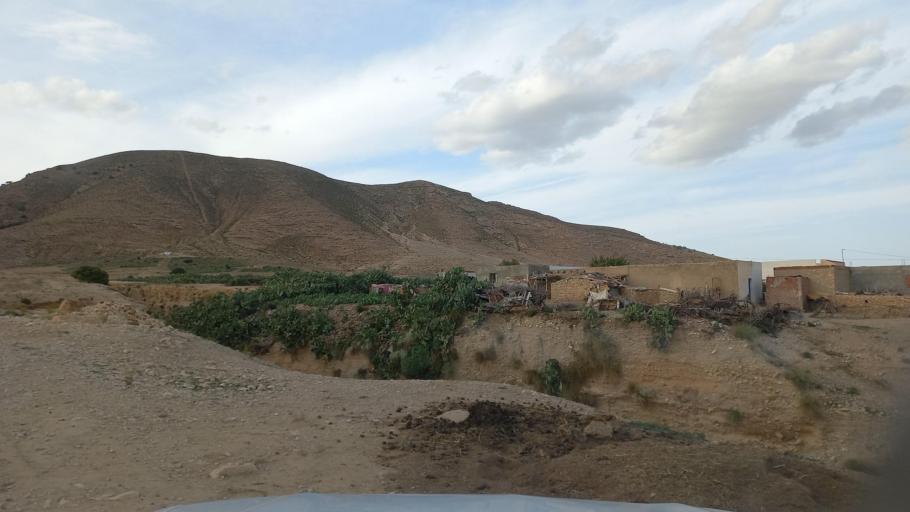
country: TN
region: Al Qasrayn
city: Sbiba
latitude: 35.4506
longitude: 9.0636
